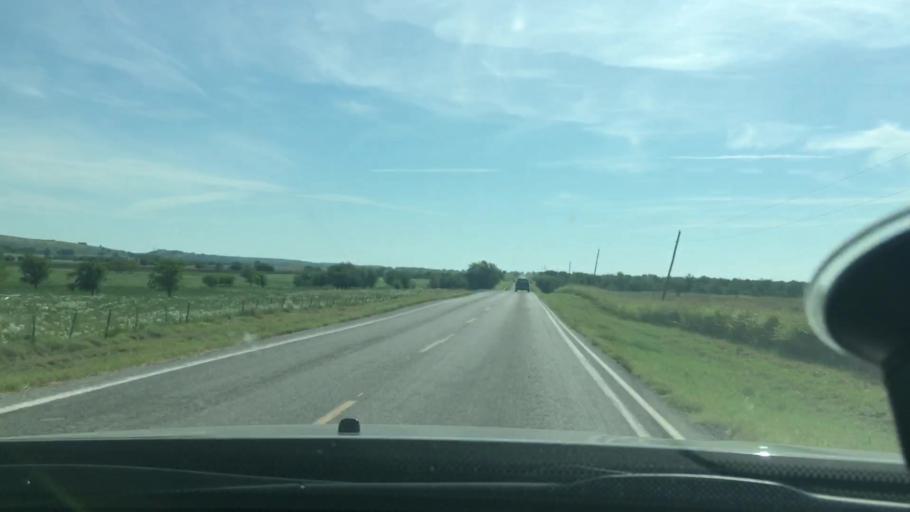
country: US
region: Oklahoma
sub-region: Carter County
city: Lone Grove
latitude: 34.3327
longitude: -97.2727
